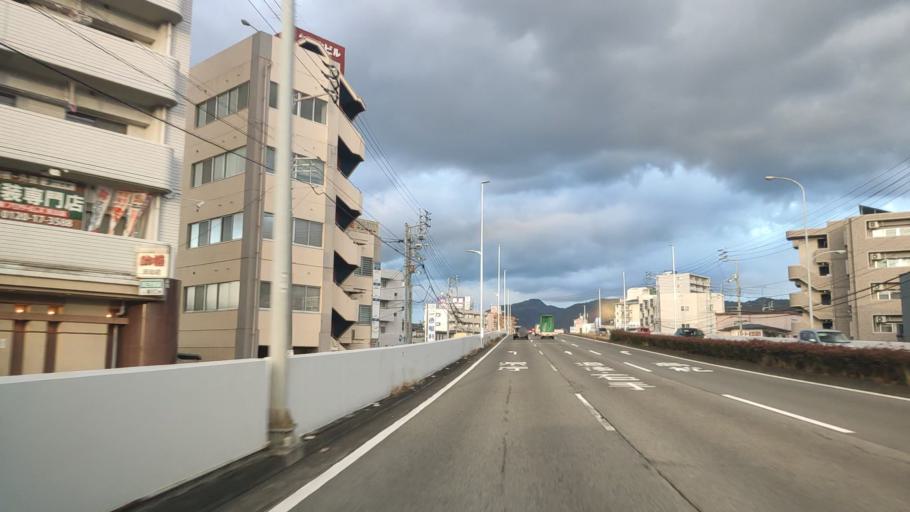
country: JP
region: Ehime
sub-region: Shikoku-chuo Shi
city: Matsuyama
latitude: 33.8243
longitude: 132.7796
